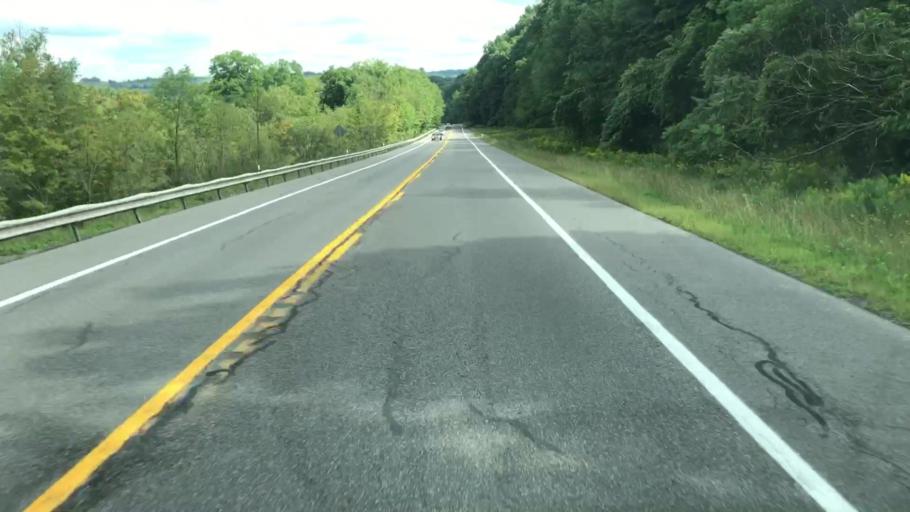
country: US
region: New York
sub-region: Onondaga County
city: Marcellus
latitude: 42.9535
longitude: -76.3652
